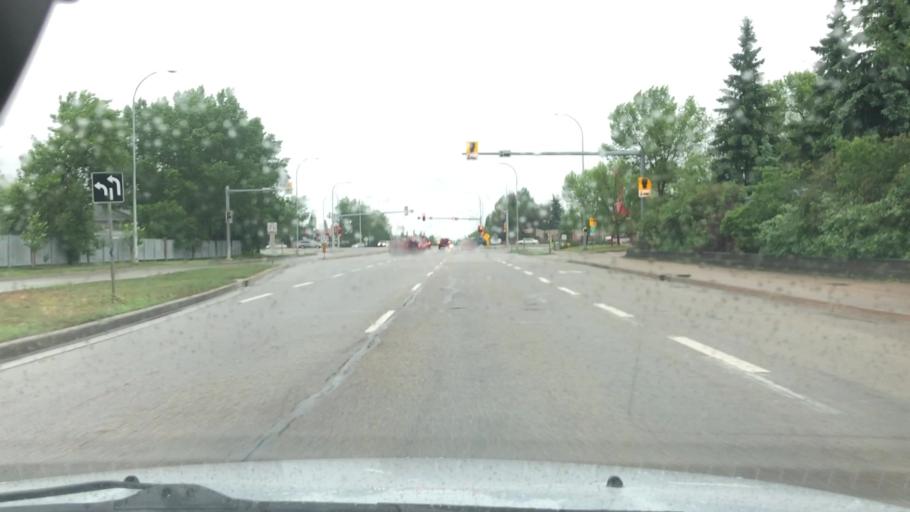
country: CA
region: Alberta
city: Sherwood Park
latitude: 53.5396
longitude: -113.2633
